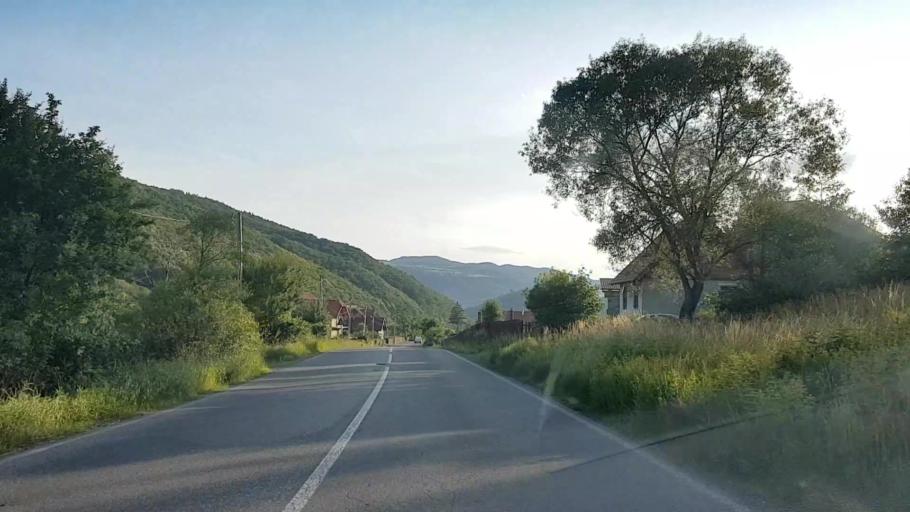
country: RO
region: Harghita
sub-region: Comuna Praid
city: Praid
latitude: 46.5642
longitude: 25.1546
